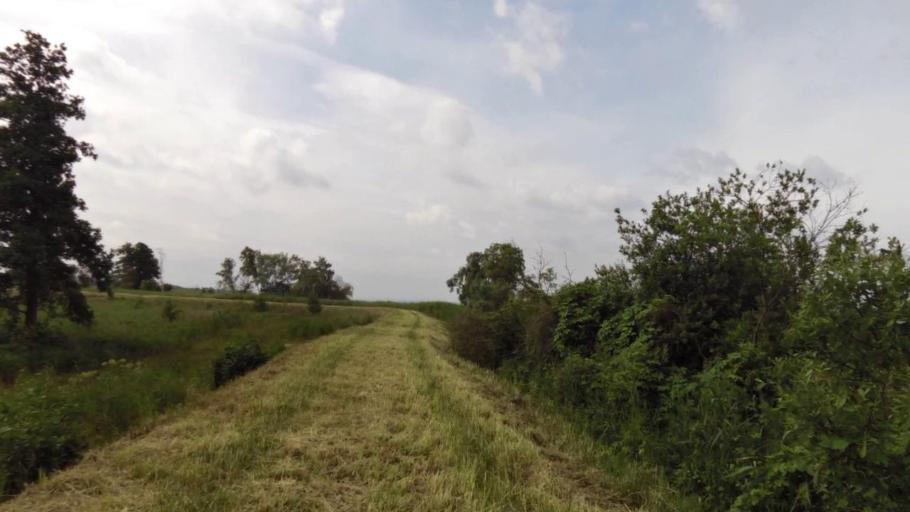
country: PL
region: West Pomeranian Voivodeship
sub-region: Powiat policki
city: Police
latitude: 53.5377
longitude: 14.6772
